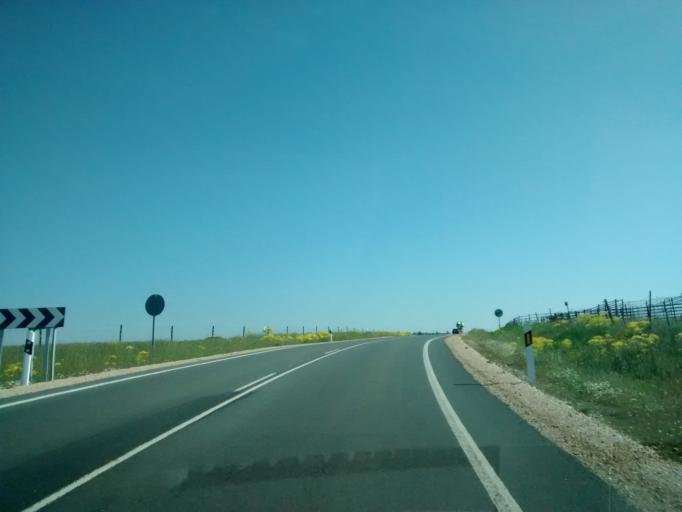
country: ES
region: Castille and Leon
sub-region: Provincia de Segovia
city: Trescasas
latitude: 40.9701
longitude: -4.0322
